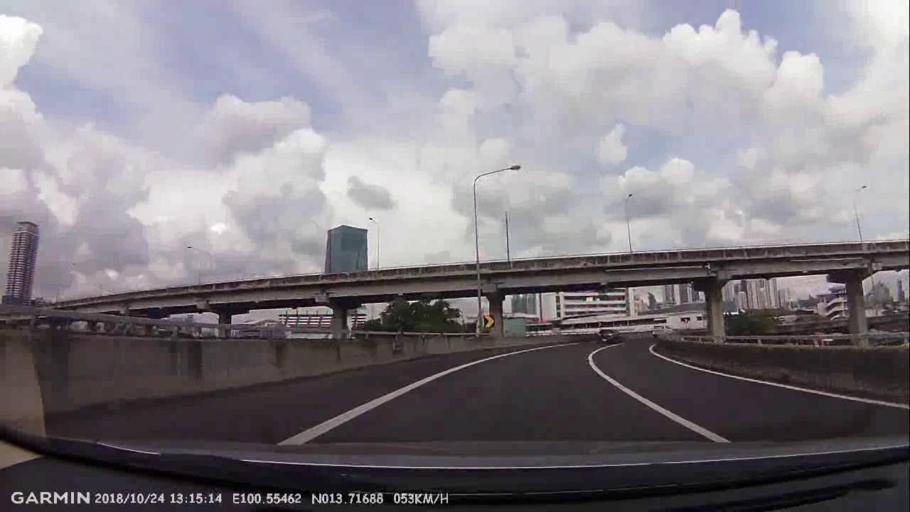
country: TH
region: Bangkok
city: Khlong Toei
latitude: 13.7169
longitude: 100.5546
